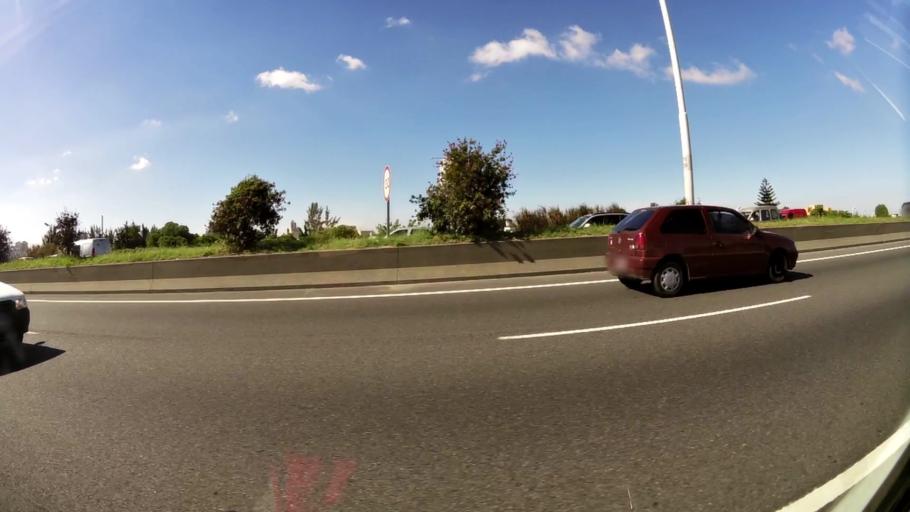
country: AR
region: Buenos Aires
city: Caseros
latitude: -34.6312
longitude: -58.5742
